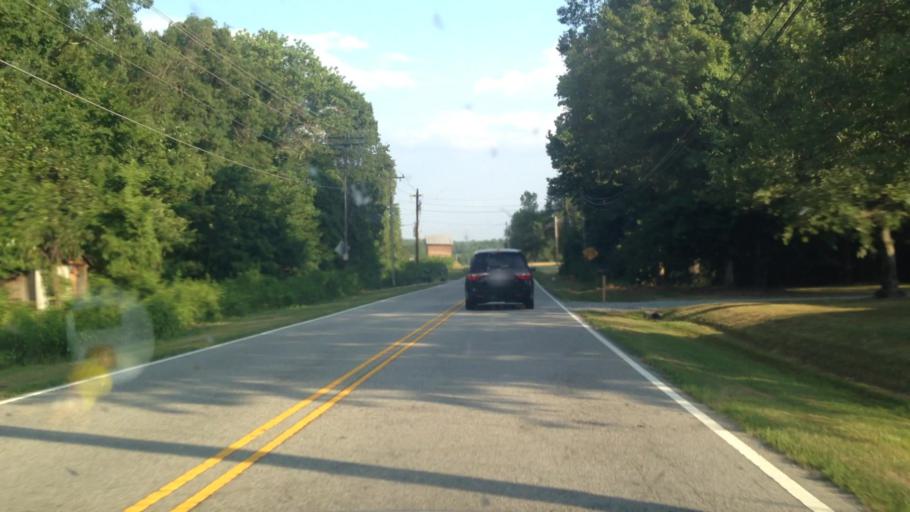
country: US
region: North Carolina
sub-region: Guilford County
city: High Point
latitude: 35.9564
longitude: -80.0728
